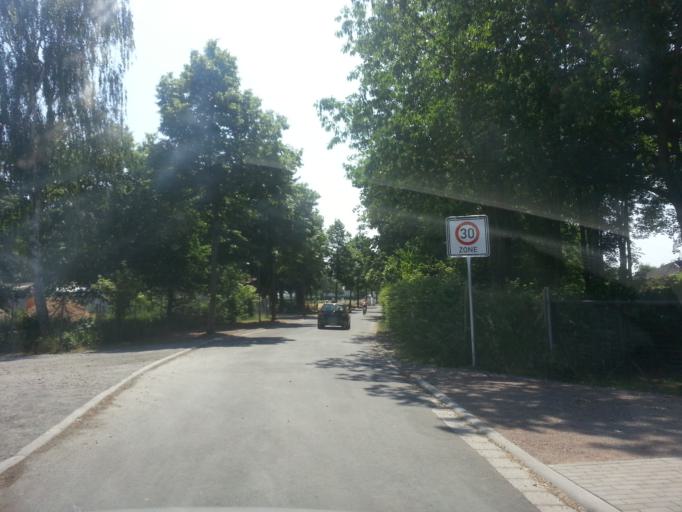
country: DE
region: Hesse
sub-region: Regierungsbezirk Darmstadt
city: Munster
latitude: 49.9326
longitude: 8.8642
